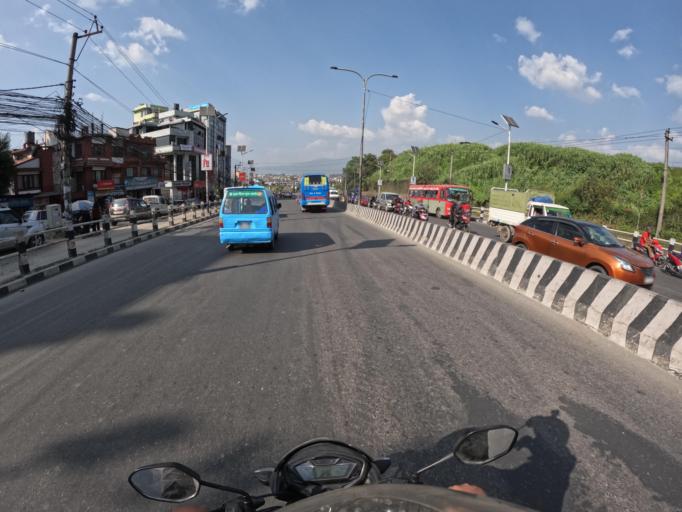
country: NP
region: Central Region
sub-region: Bagmati Zone
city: Kathmandu
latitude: 27.6823
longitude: 85.3494
